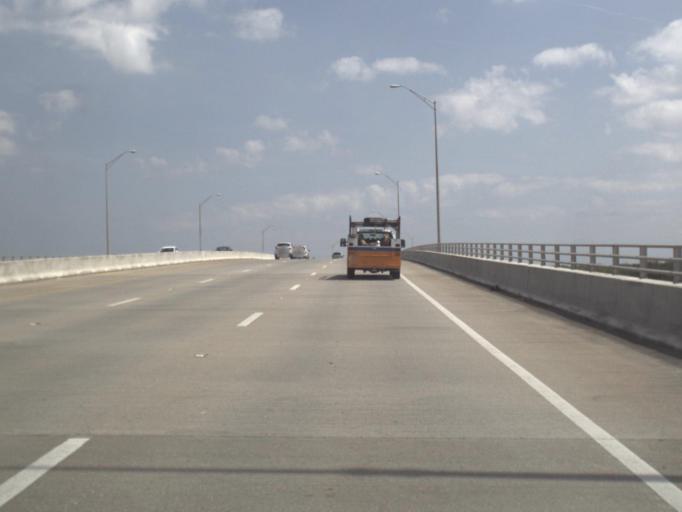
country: US
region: Florida
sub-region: Escambia County
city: Warrington
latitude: 30.4008
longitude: -87.2485
